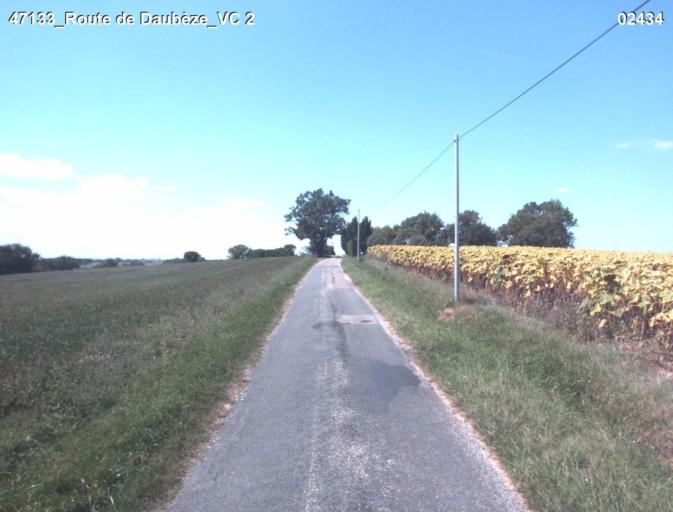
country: FR
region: Aquitaine
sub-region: Departement du Lot-et-Garonne
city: Laplume
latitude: 44.0780
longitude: 0.5615
